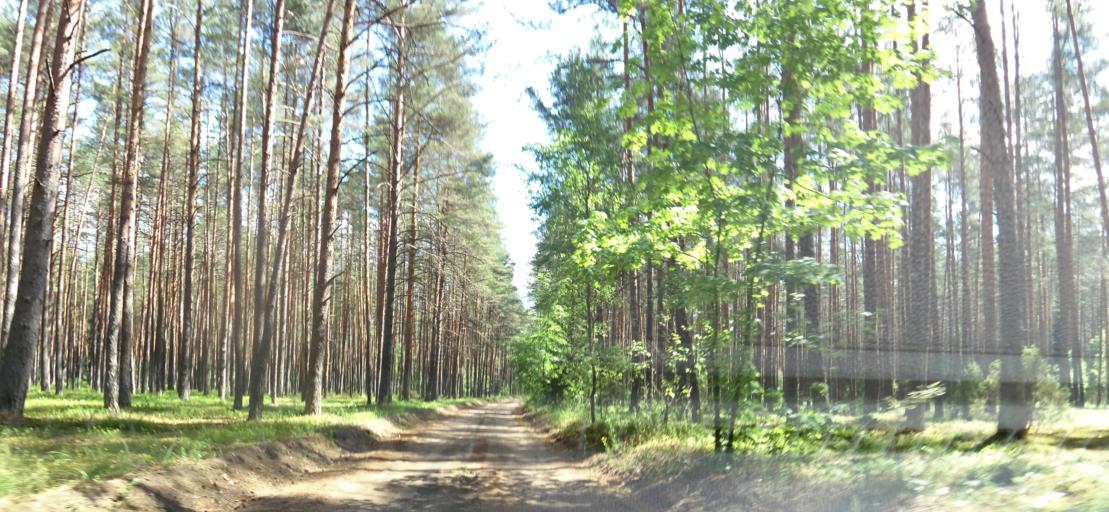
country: LT
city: Nemencine
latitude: 54.8293
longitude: 25.4240
